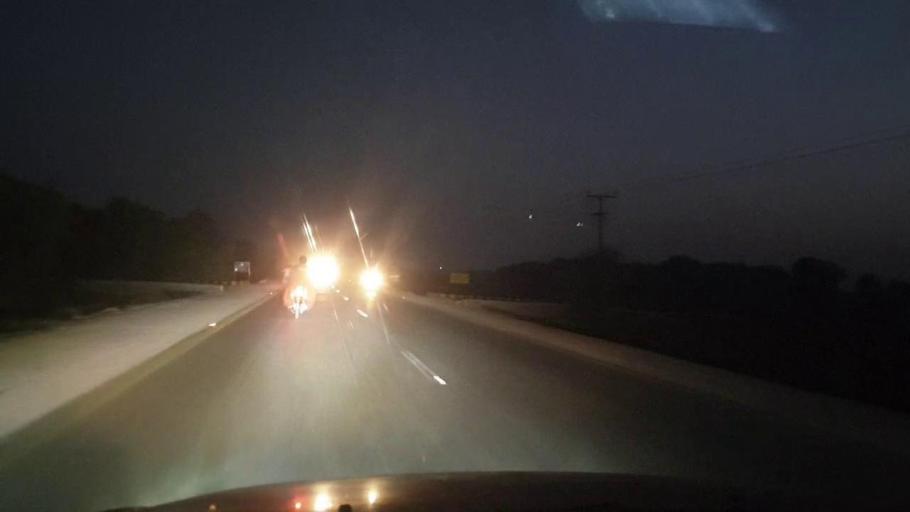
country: PK
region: Sindh
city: Chambar
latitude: 25.3079
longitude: 68.8076
